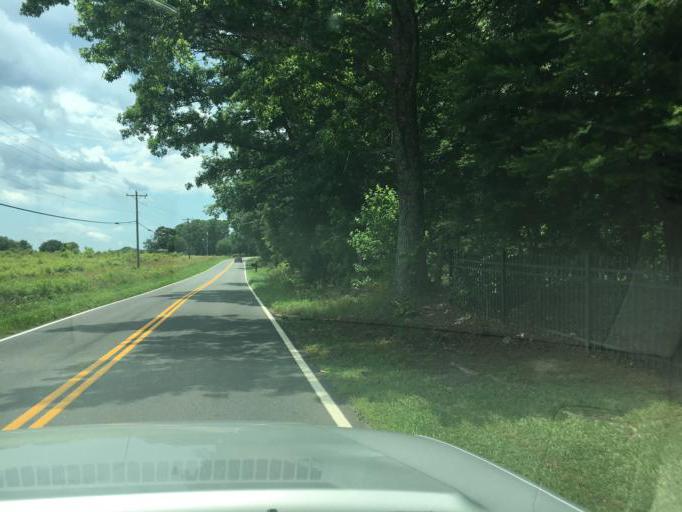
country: US
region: South Carolina
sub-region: Greenville County
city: Greer
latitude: 34.8722
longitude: -82.2063
